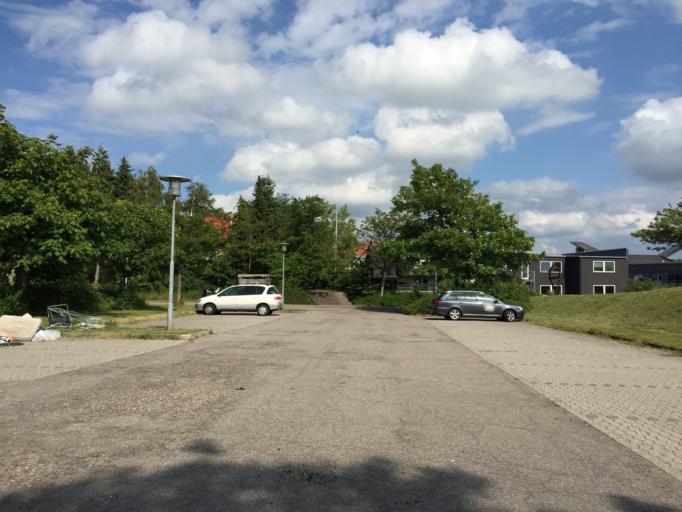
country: DK
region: Capital Region
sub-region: Gribskov Kommune
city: Helsinge
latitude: 56.0210
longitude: 12.1981
